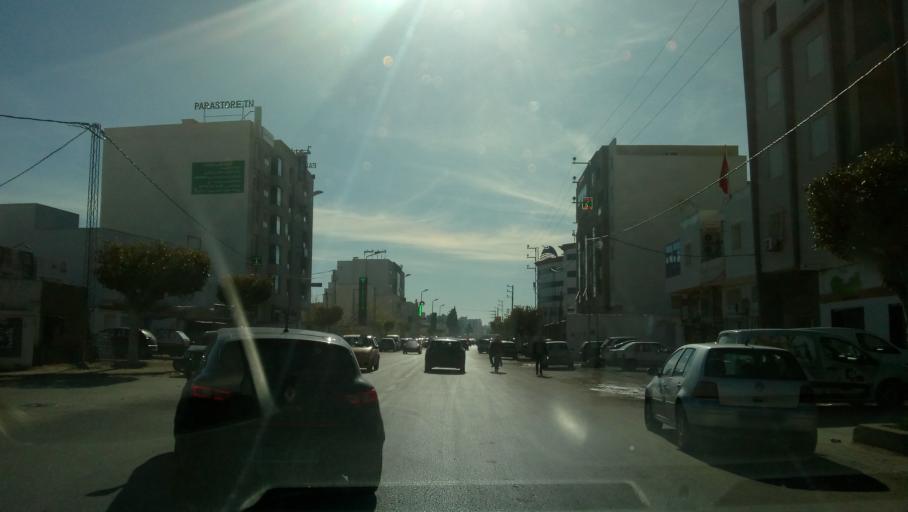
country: TN
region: Safaqis
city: Sfax
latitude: 34.7483
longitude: 10.7369
